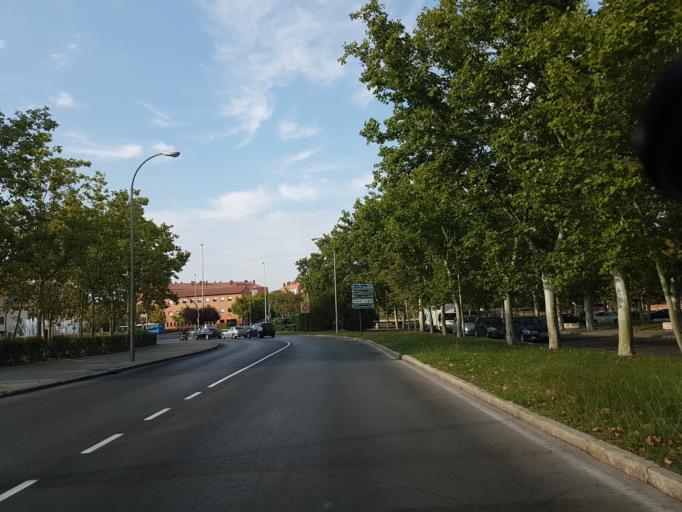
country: ES
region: Madrid
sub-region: Provincia de Madrid
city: Moratalaz
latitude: 40.4262
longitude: -3.6470
